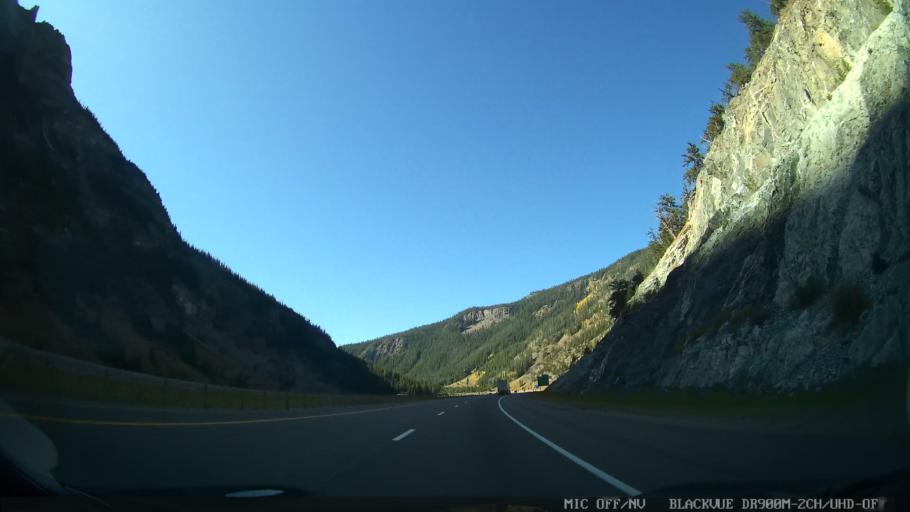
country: US
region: Colorado
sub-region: Summit County
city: Frisco
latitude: 39.5259
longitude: -106.1396
